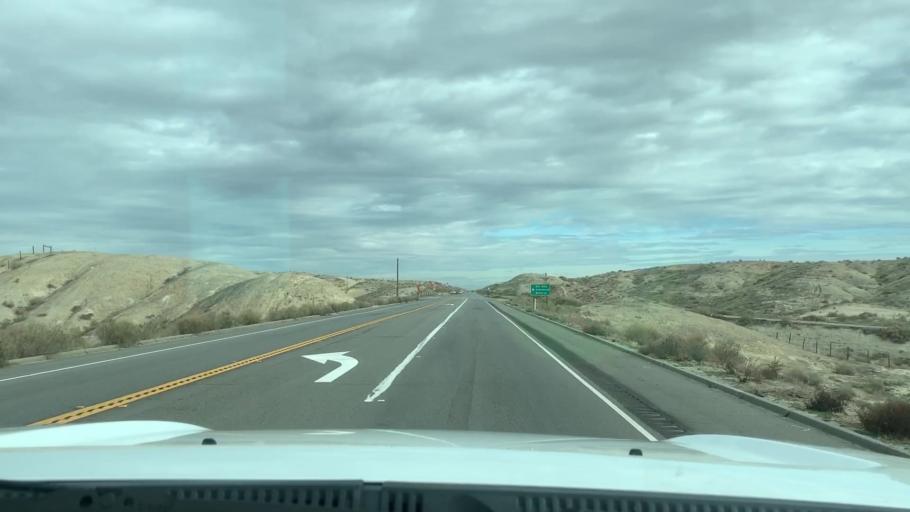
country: US
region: California
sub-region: Kern County
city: Ford City
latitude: 35.2381
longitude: -119.3611
